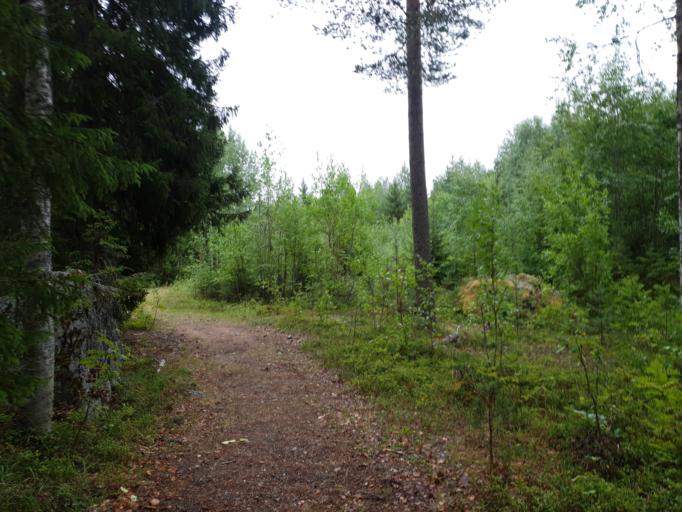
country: SE
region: Vaesterbotten
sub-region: Skelleftea Kommun
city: Viken
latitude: 64.8003
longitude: 20.7387
